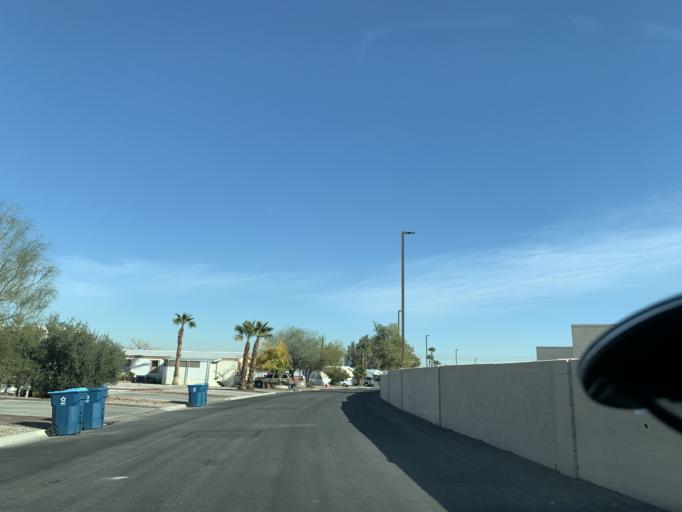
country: US
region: Nevada
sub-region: Clark County
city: Spring Valley
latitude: 36.1018
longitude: -115.2276
